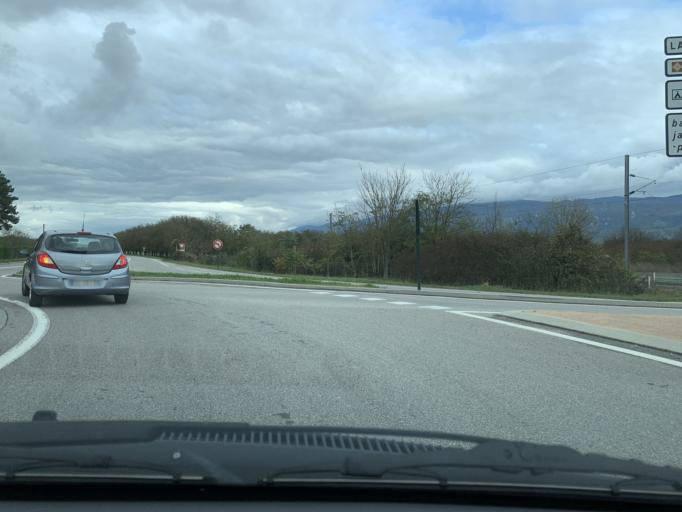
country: FR
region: Rhone-Alpes
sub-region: Departement de l'Isere
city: Chatte
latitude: 45.1246
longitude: 5.2805
